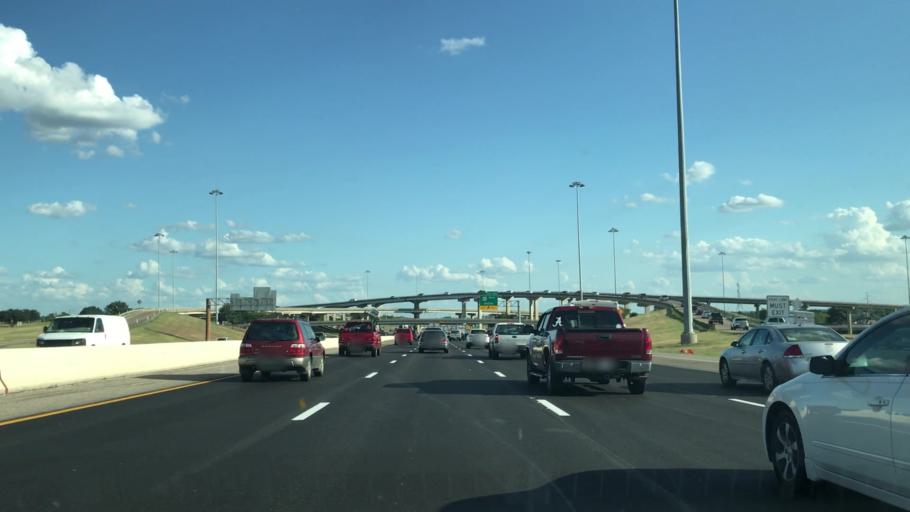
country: US
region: Texas
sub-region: Dallas County
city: Mesquite
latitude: 32.7969
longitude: -96.6259
